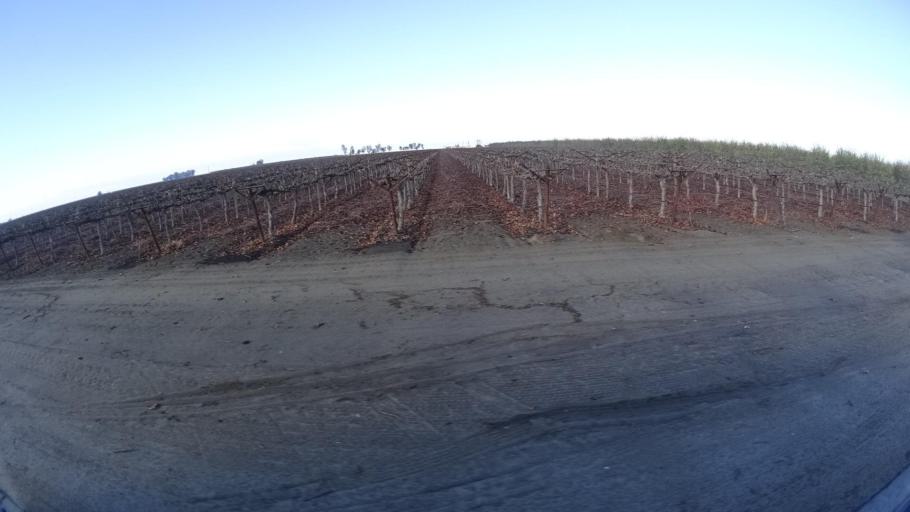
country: US
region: California
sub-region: Kern County
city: Delano
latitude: 35.7392
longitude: -119.3301
